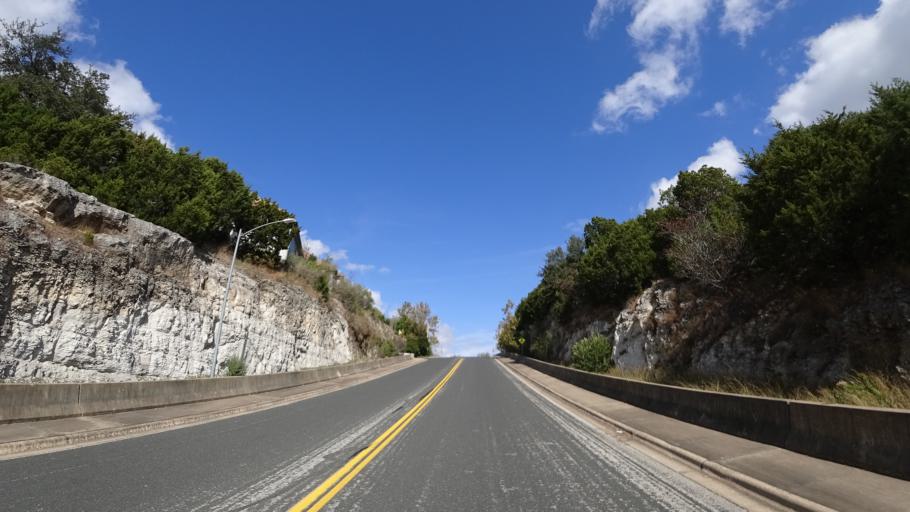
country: US
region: Texas
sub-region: Williamson County
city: Jollyville
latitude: 30.4218
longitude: -97.7904
